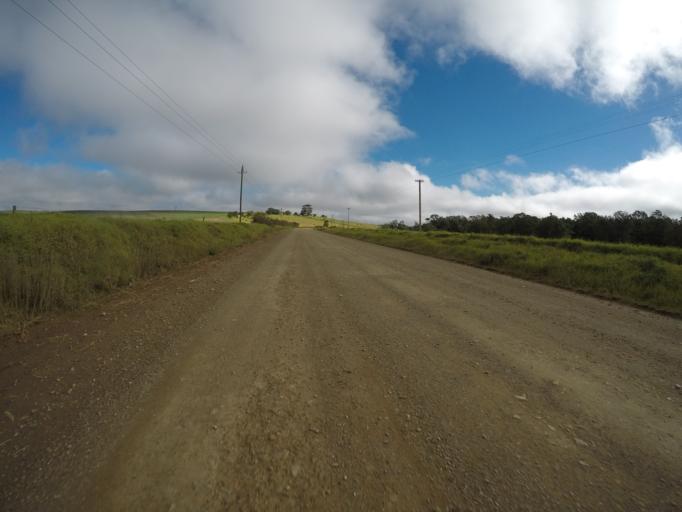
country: ZA
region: Western Cape
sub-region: Cape Winelands District Municipality
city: Ashton
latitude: -34.1307
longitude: 19.8487
